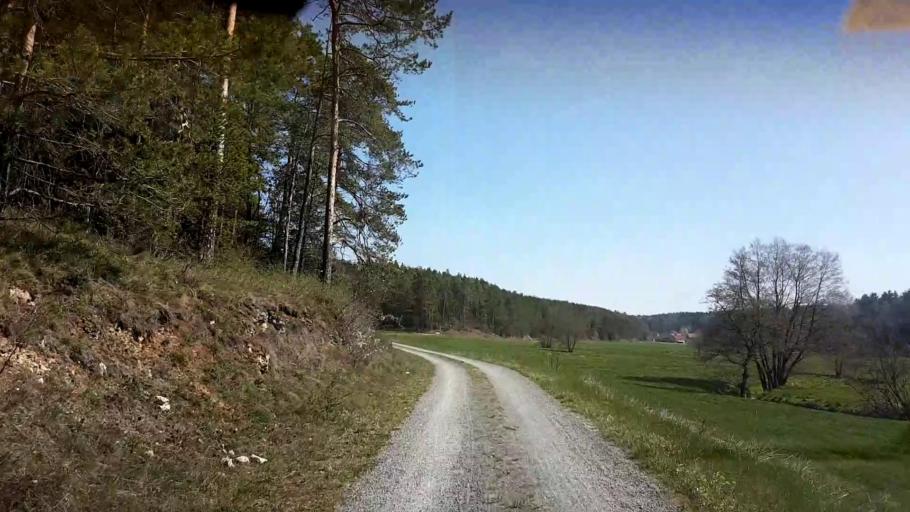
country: DE
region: Bavaria
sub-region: Upper Franconia
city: Konigsfeld
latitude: 49.9377
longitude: 11.1938
